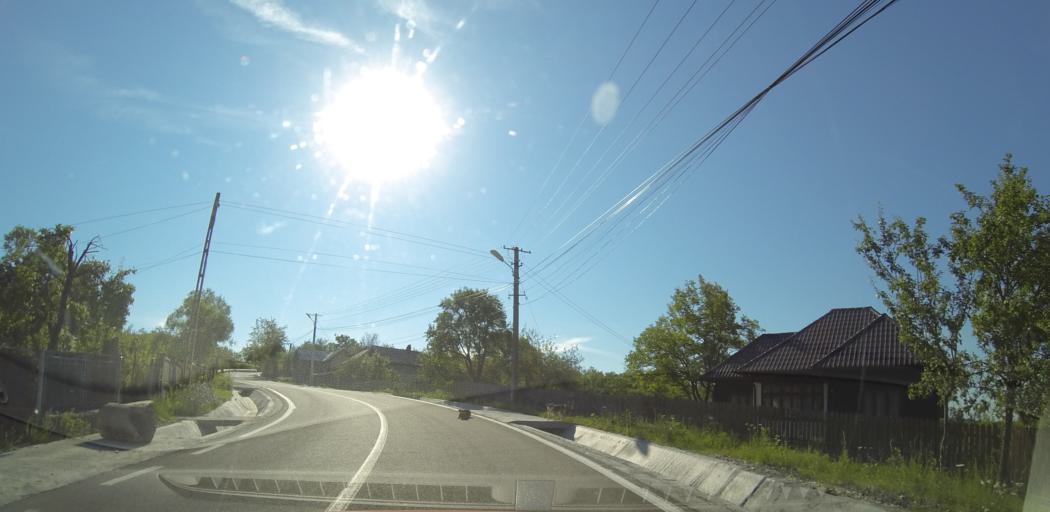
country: RO
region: Valcea
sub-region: Comuna Vaideeni
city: Vaideeni
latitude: 45.1749
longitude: 23.8702
